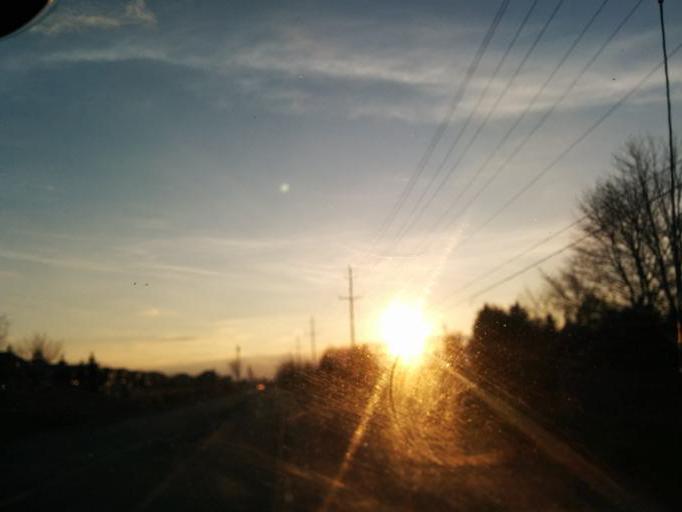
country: CA
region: Ontario
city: Brampton
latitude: 43.8737
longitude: -79.7641
